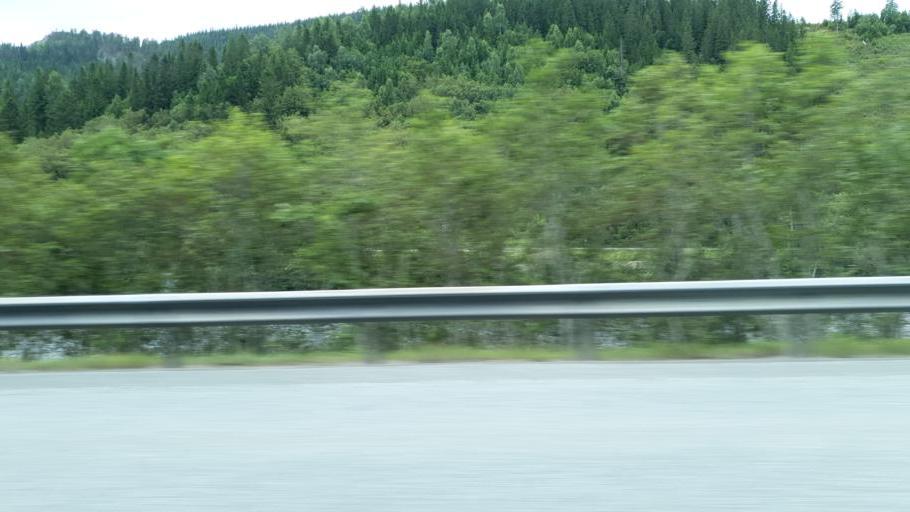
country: NO
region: Sor-Trondelag
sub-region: Midtre Gauldal
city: Storen
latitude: 63.0603
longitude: 10.2904
